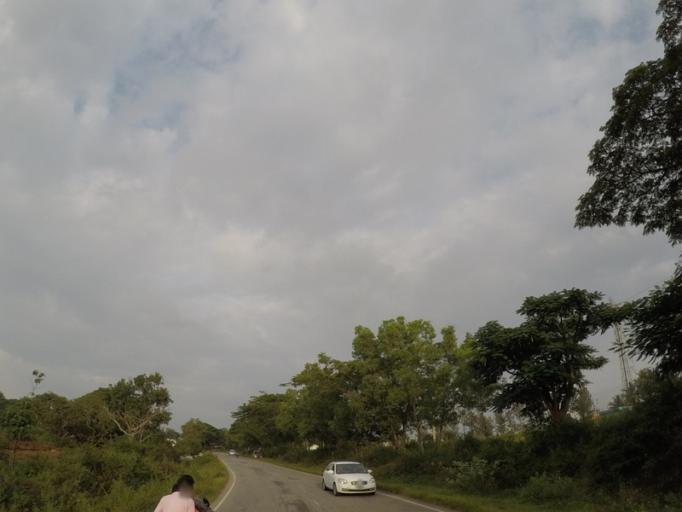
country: IN
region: Karnataka
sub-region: Hassan
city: Belur
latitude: 13.2215
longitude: 75.8579
